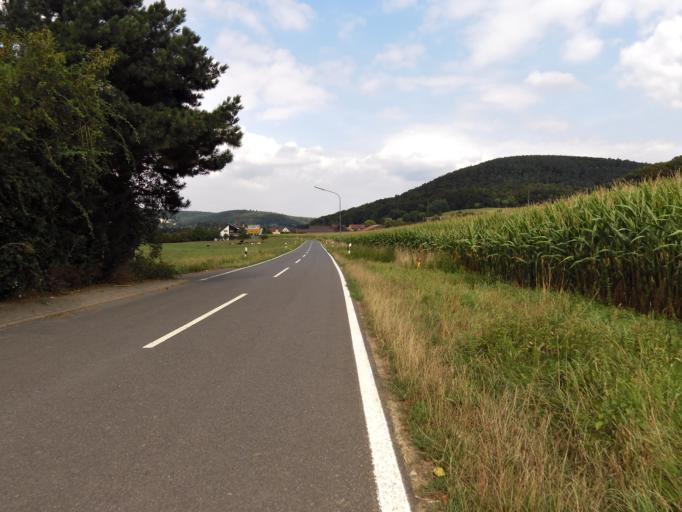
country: DE
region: Hesse
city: Hochst im Odenwald
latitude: 49.8014
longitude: 9.0058
